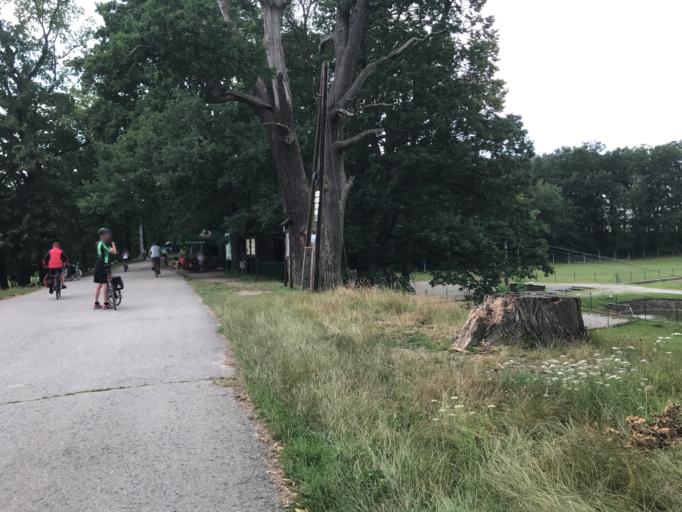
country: CZ
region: Jihocesky
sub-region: Okres Jindrichuv Hradec
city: Trebon
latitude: 49.0481
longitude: 14.7615
